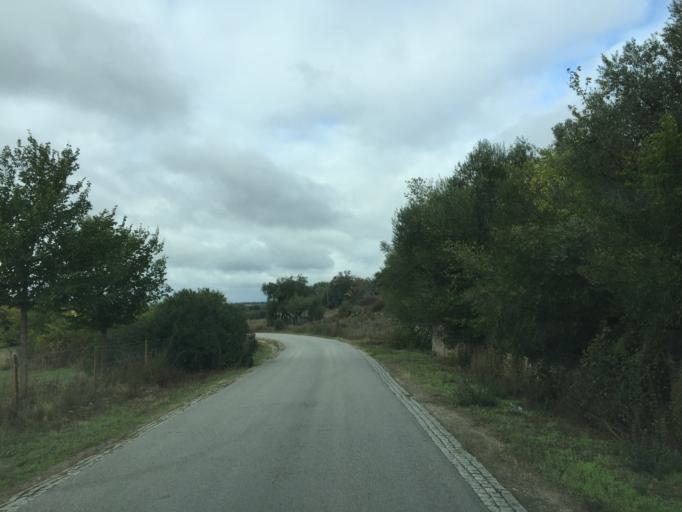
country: PT
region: Portalegre
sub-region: Alter do Chao
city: Alter do Chao
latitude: 39.2205
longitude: -7.6792
